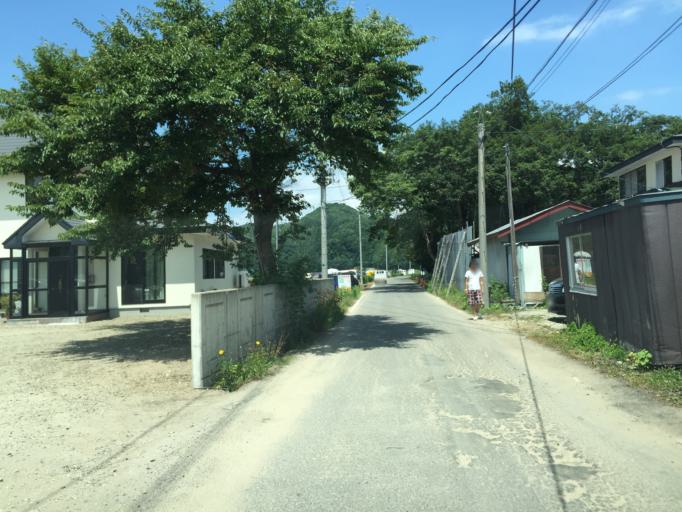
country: JP
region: Fukushima
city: Inawashiro
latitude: 37.4613
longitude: 140.0462
